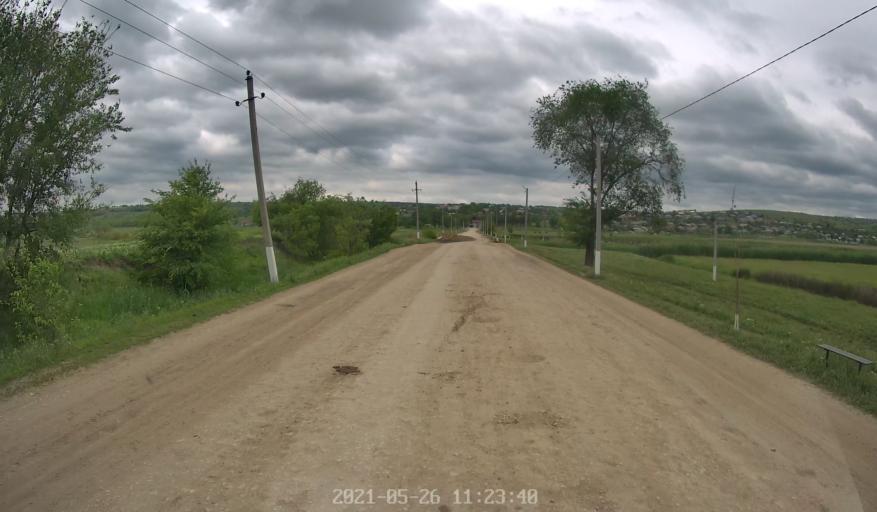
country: MD
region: Hincesti
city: Dancu
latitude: 46.8237
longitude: 28.3768
